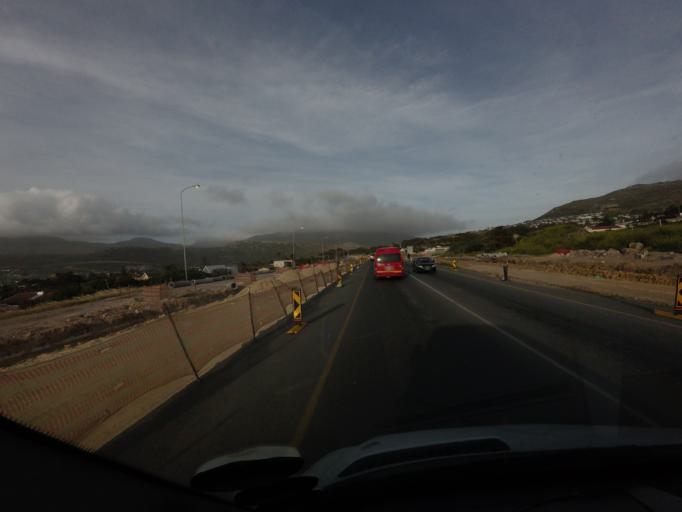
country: ZA
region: Western Cape
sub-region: City of Cape Town
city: Constantia
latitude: -34.1297
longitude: 18.3906
